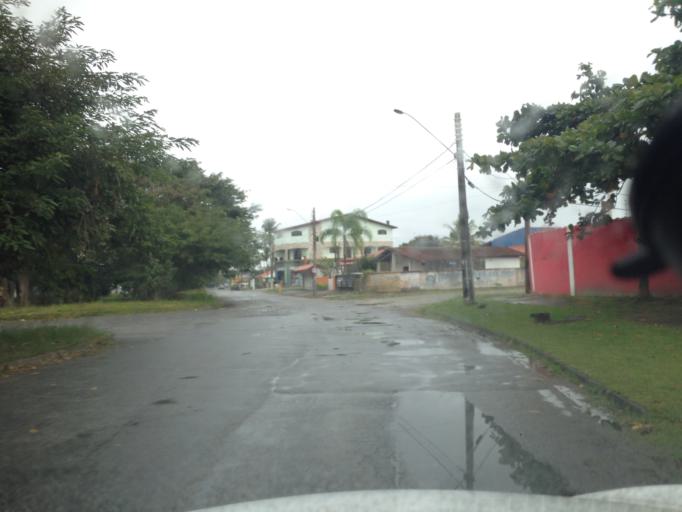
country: BR
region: Sao Paulo
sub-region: Itanhaem
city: Itanhaem
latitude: -24.2299
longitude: -46.8737
